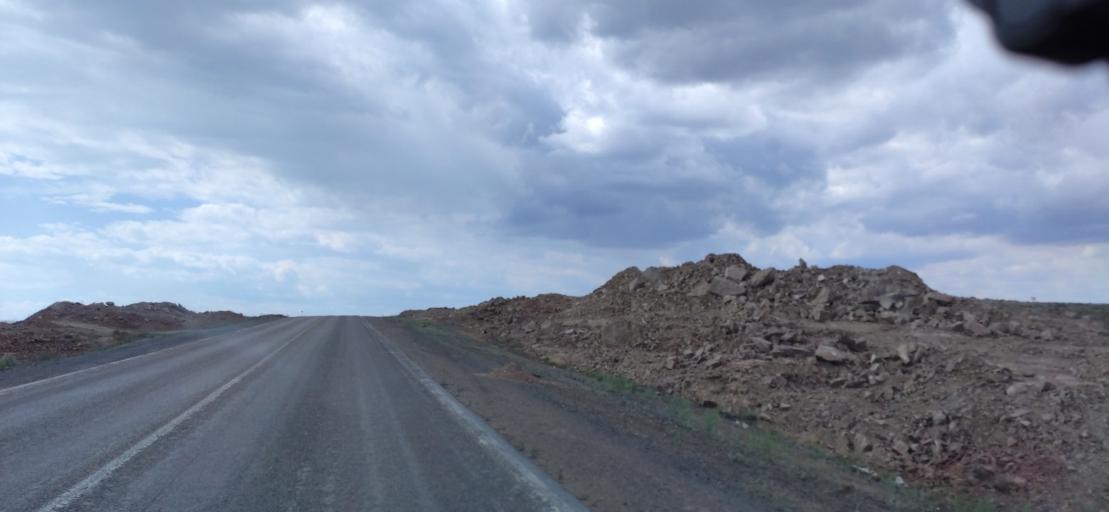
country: KZ
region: Qaraghandy
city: Saryshaghan
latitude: 46.0837
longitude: 73.6055
